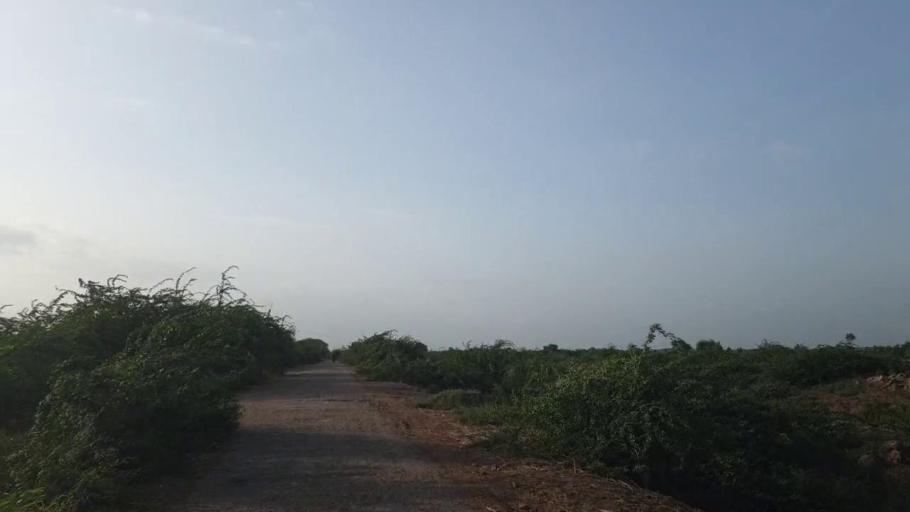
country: PK
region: Sindh
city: Kadhan
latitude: 24.6314
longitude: 69.1587
